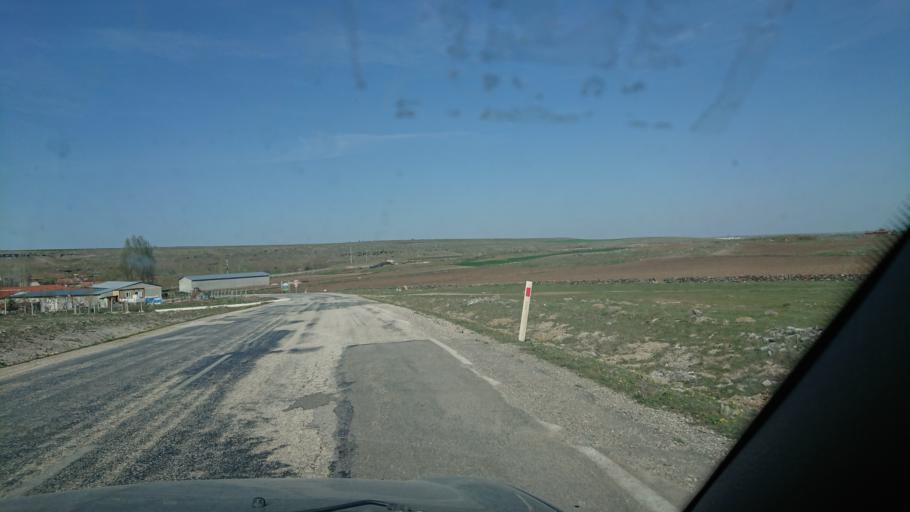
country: TR
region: Eskisehir
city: Eskisehir
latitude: 39.6755
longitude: 30.4835
